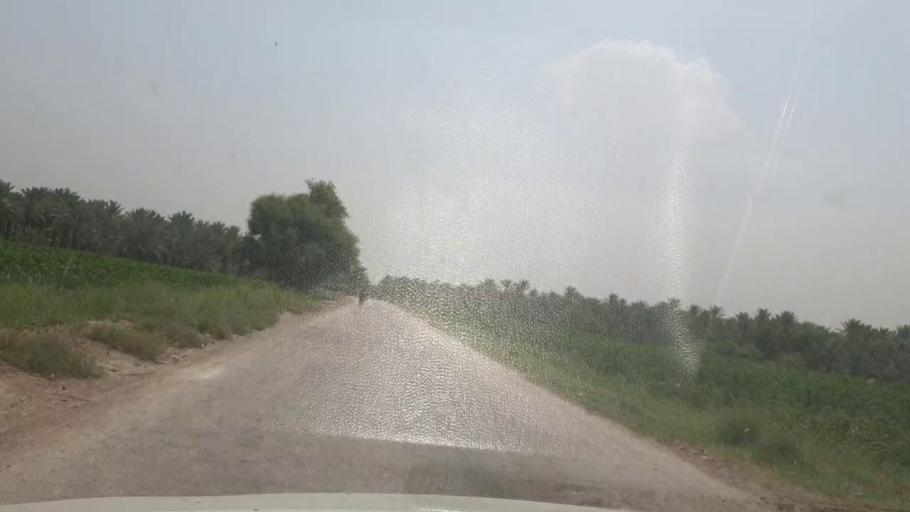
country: PK
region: Sindh
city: Kot Diji
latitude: 27.3738
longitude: 68.7144
